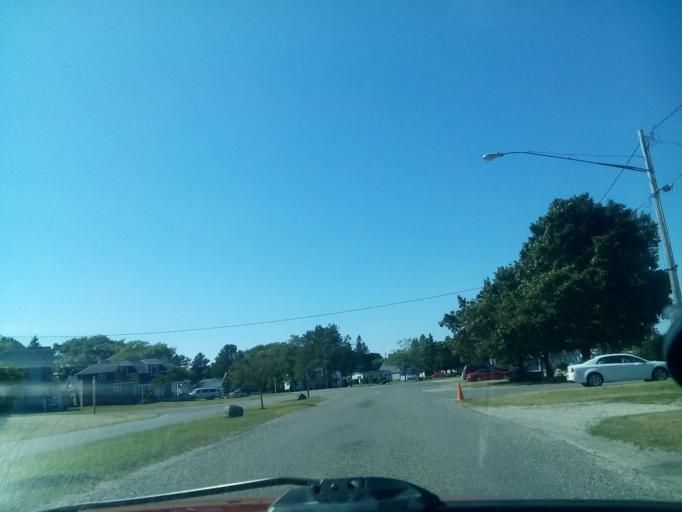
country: US
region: Michigan
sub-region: Mackinac County
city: Saint Ignace
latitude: 45.7842
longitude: -84.7246
